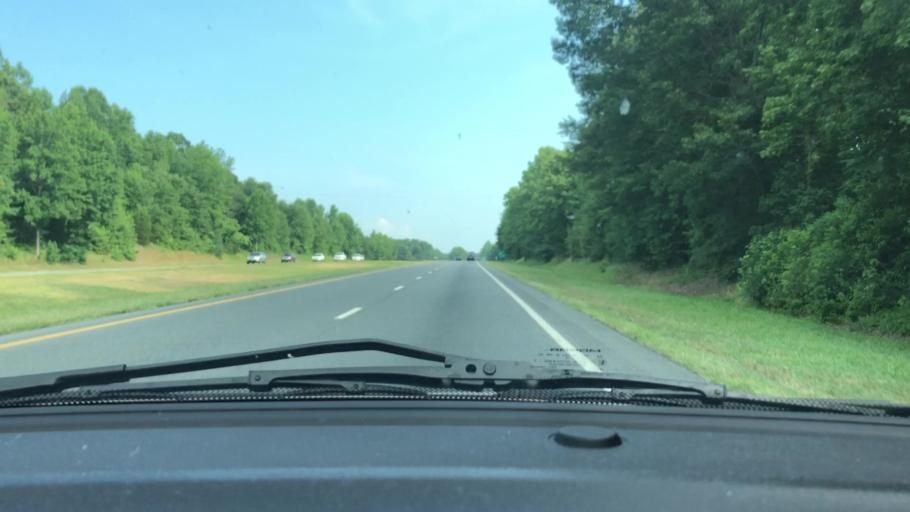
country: US
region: North Carolina
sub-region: Guilford County
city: Forest Oaks
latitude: 35.9234
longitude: -79.6791
